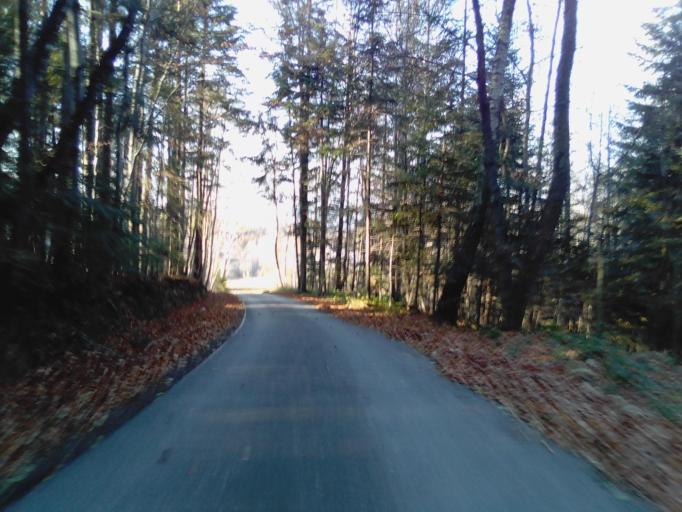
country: PL
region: Subcarpathian Voivodeship
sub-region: Powiat strzyzowski
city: Gwoznica Gorna
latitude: 49.8301
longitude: 21.9778
